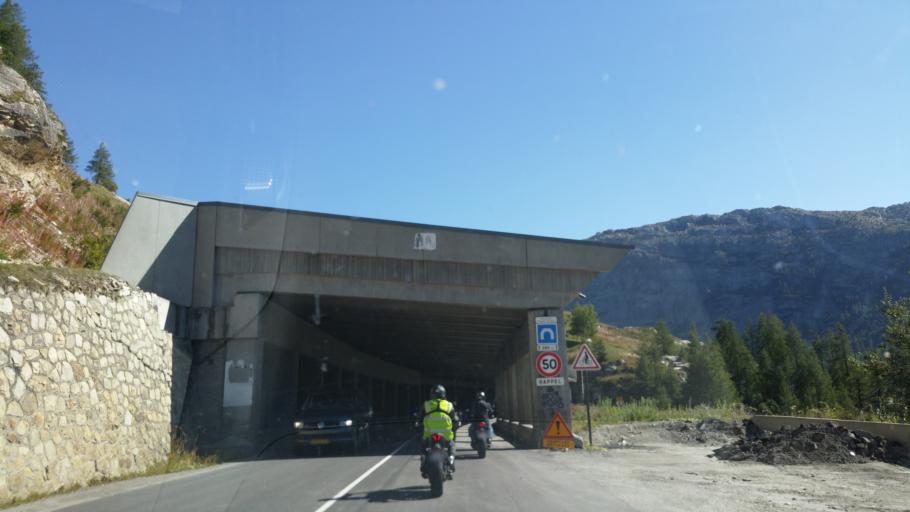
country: FR
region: Rhone-Alpes
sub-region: Departement de la Savoie
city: Tignes
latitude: 45.4852
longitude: 6.9446
